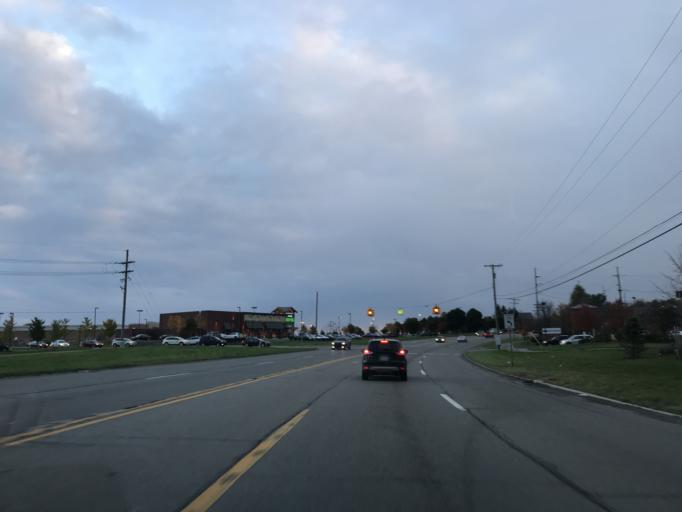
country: US
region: Michigan
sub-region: Wayne County
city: Northville
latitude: 42.4359
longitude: -83.4345
